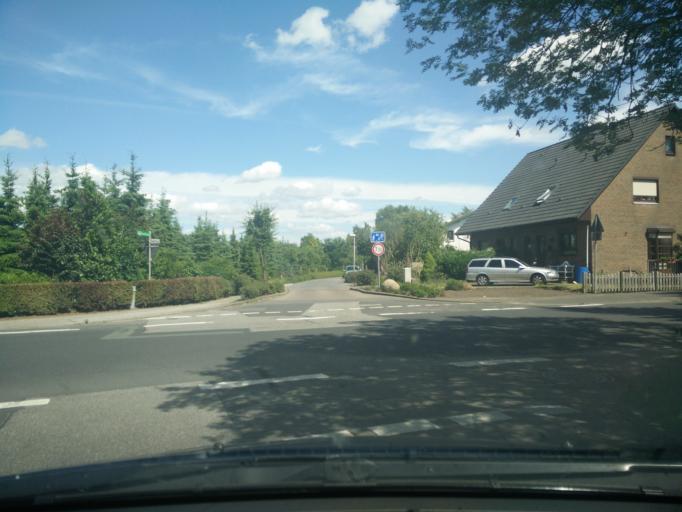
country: DE
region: Schleswig-Holstein
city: Tornesch
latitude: 53.6895
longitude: 9.7238
